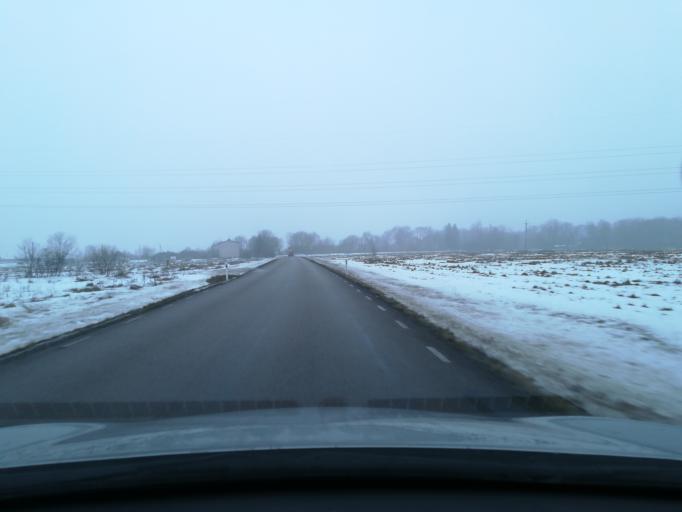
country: EE
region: Harju
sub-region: Rae vald
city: Jueri
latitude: 59.3775
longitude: 24.8940
